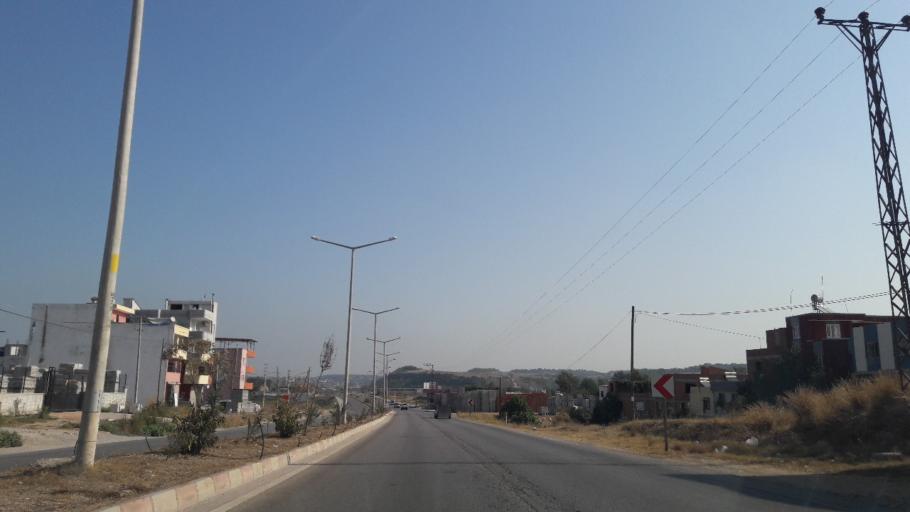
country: TR
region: Adana
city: Yuregir
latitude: 37.0466
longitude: 35.4361
